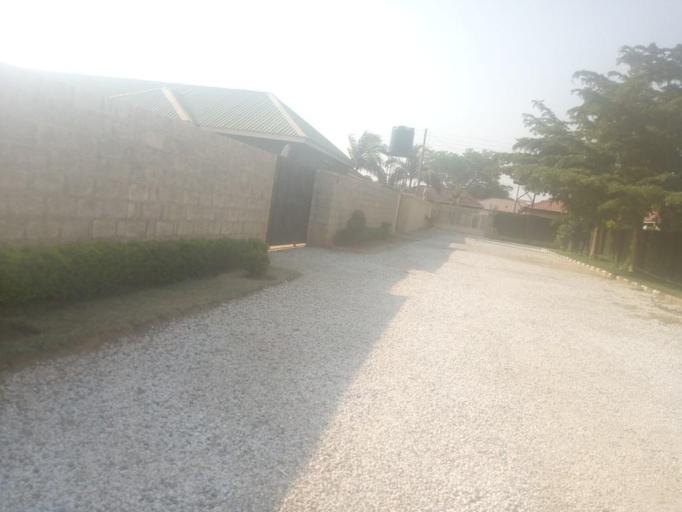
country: ZM
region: Lusaka
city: Lusaka
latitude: -15.4001
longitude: 28.3889
